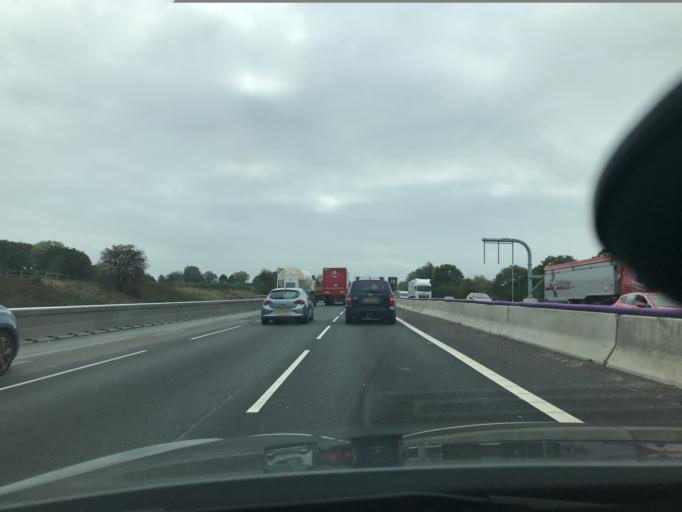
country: GB
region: England
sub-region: Cheshire East
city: Holmes Chapel
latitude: 53.1771
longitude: -2.3640
